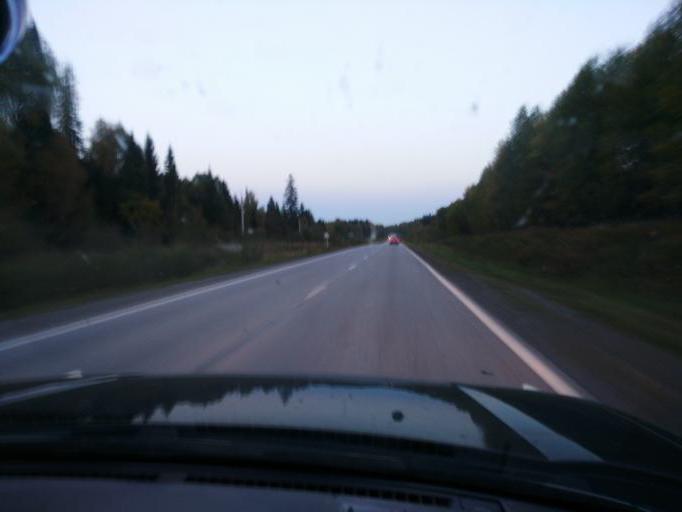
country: RU
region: Perm
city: Verkhnechusovskiye Gorodki
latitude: 58.2536
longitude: 57.0056
